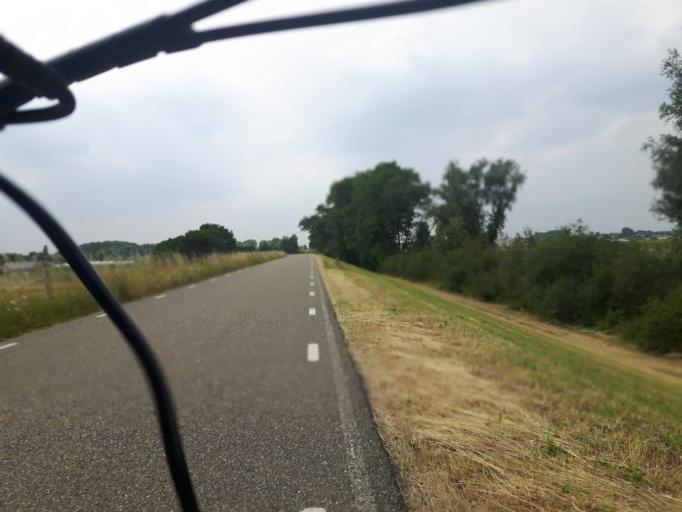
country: NL
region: North Brabant
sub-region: Gemeente Aalburg
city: Aalburg
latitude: 51.8139
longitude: 5.1147
